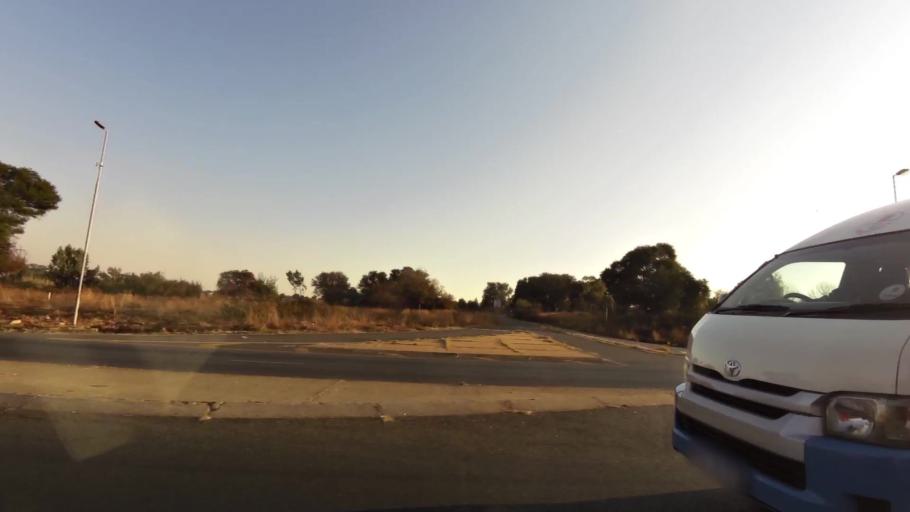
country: ZA
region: Gauteng
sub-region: City of Johannesburg Metropolitan Municipality
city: Soweto
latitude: -26.2720
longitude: 27.9588
